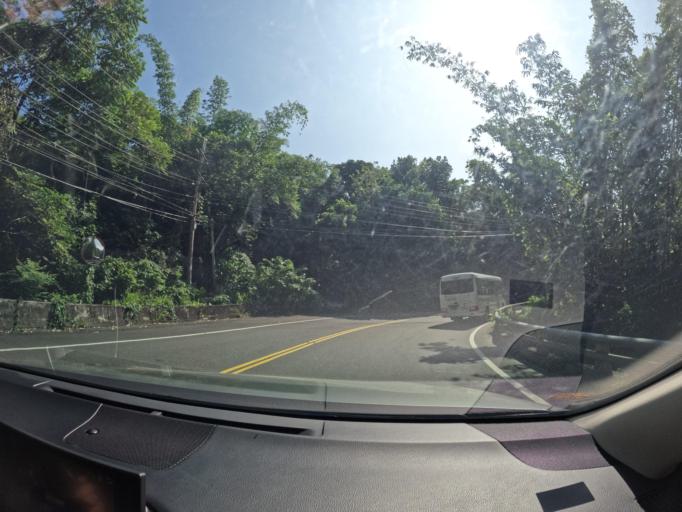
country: TW
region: Taiwan
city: Yujing
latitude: 23.0708
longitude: 120.6551
